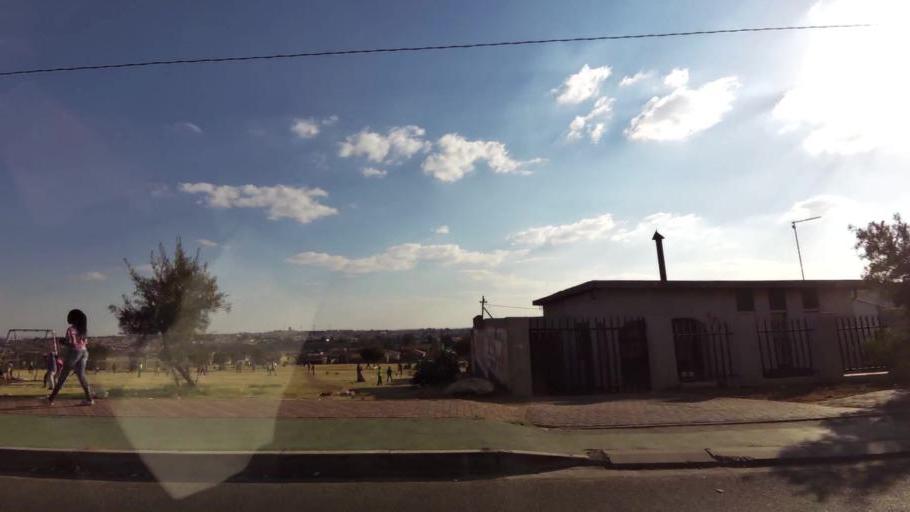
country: ZA
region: Gauteng
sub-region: City of Johannesburg Metropolitan Municipality
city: Roodepoort
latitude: -26.2174
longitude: 27.8856
